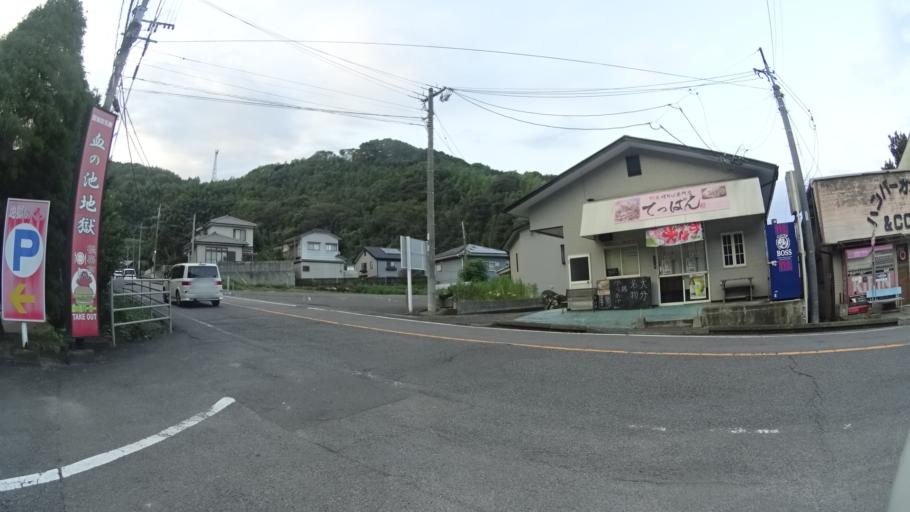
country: JP
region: Oita
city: Beppu
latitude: 33.3276
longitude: 131.4788
